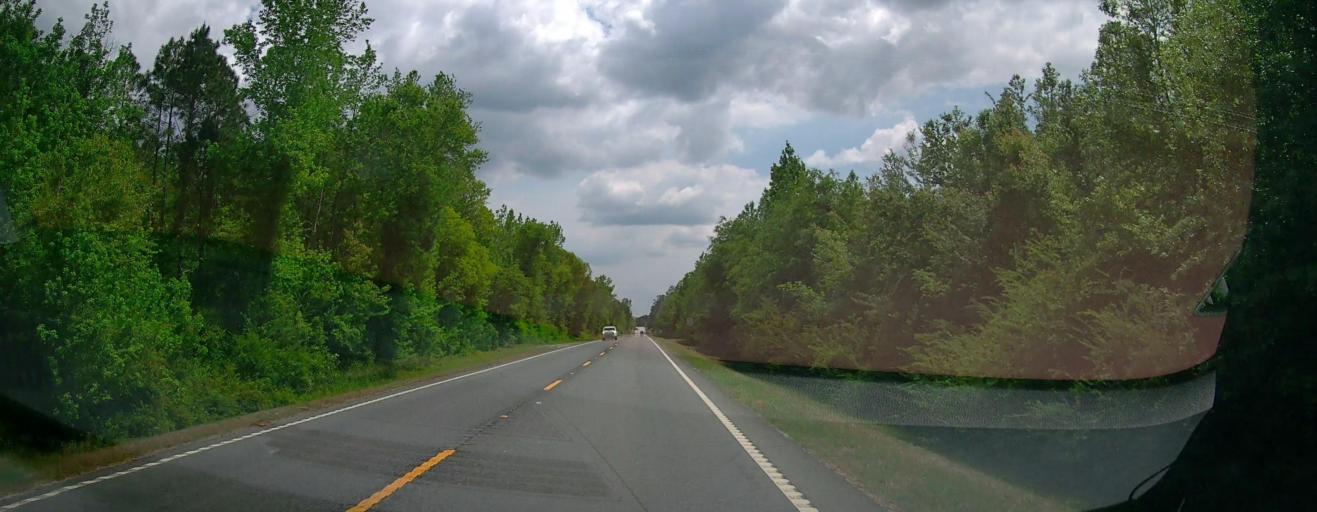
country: US
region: Georgia
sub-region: Treutlen County
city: Soperton
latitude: 32.3930
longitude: -82.6008
